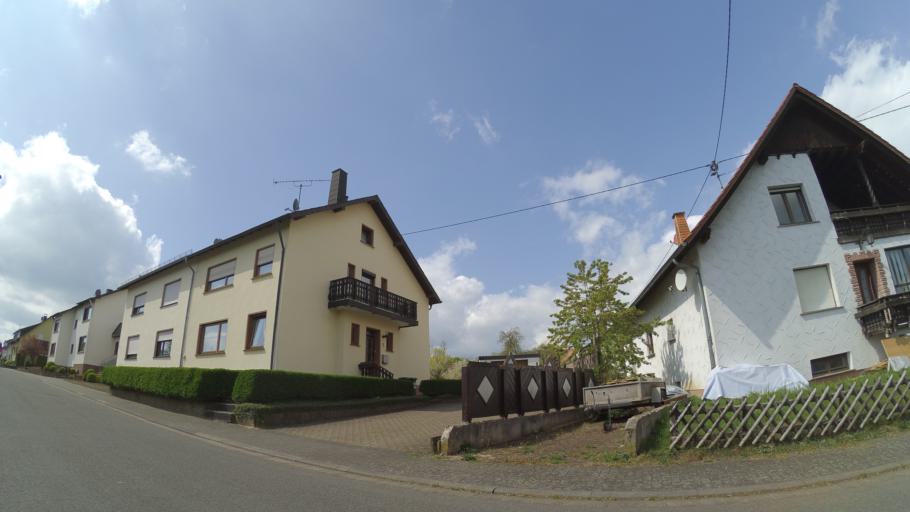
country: DE
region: Saarland
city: Wadern
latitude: 49.5423
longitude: 6.8870
